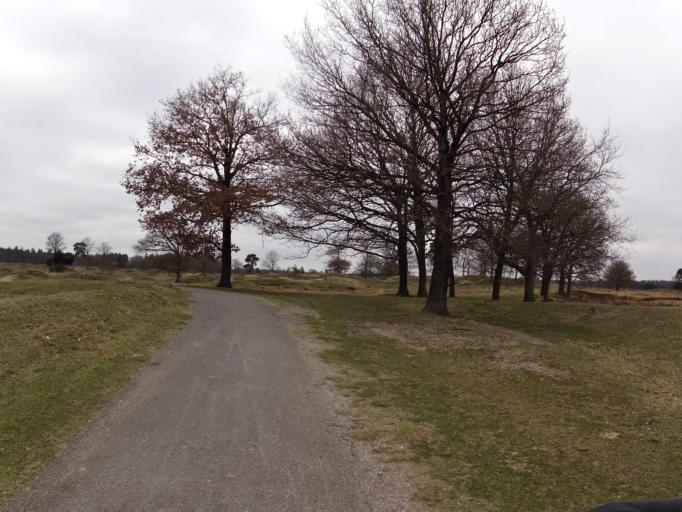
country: NL
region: Drenthe
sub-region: Gemeente Westerveld
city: Dwingeloo
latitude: 52.9246
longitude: 6.2938
